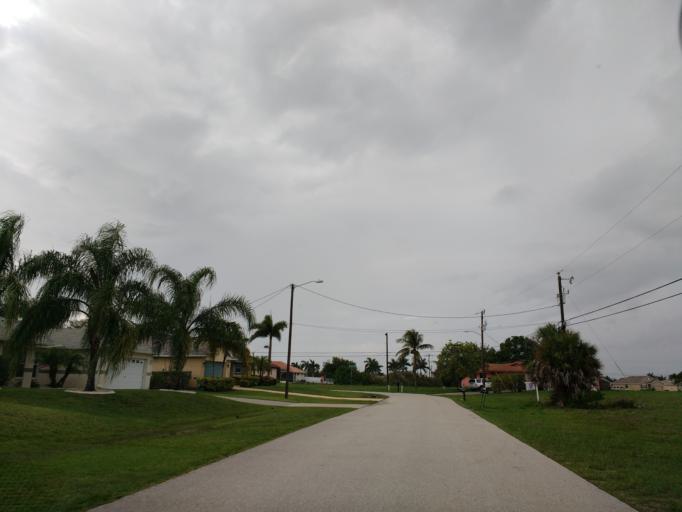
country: US
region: Florida
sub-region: Lee County
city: Cape Coral
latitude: 26.6006
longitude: -82.0239
